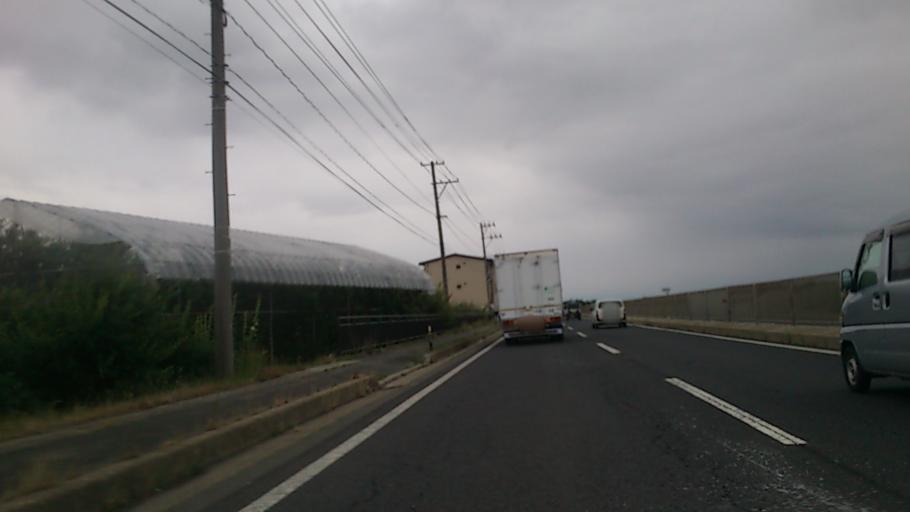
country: JP
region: Yamagata
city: Higashine
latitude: 38.4126
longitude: 140.3745
